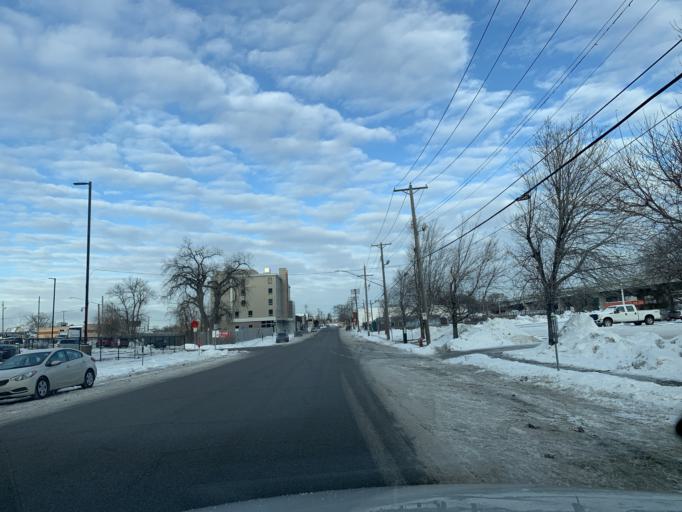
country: US
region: Minnesota
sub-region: Hennepin County
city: Minneapolis
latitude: 44.9860
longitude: -93.2814
